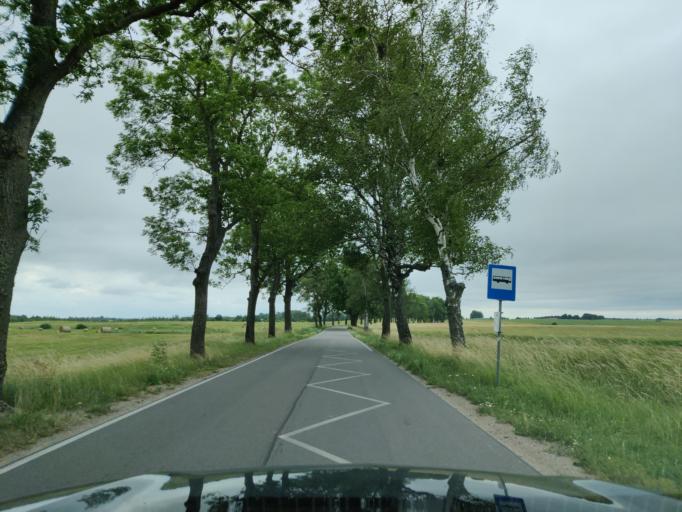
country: PL
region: Warmian-Masurian Voivodeship
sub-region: Powiat mragowski
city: Mikolajki
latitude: 53.8726
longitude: 21.5957
